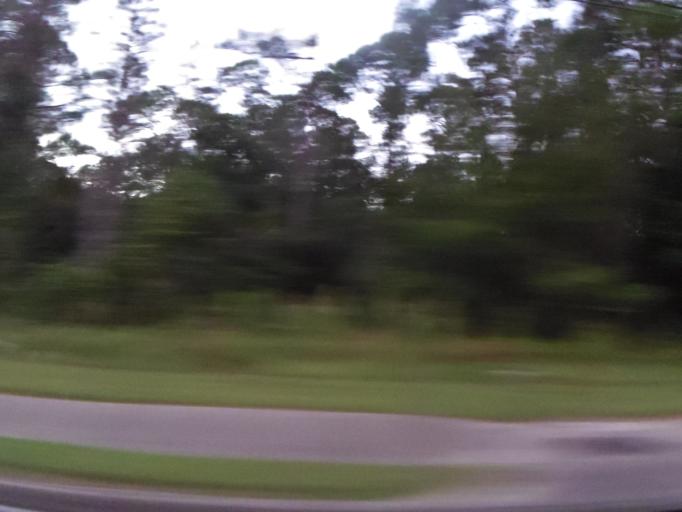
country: US
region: Florida
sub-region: Saint Johns County
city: Palm Valley
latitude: 30.0694
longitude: -81.4924
